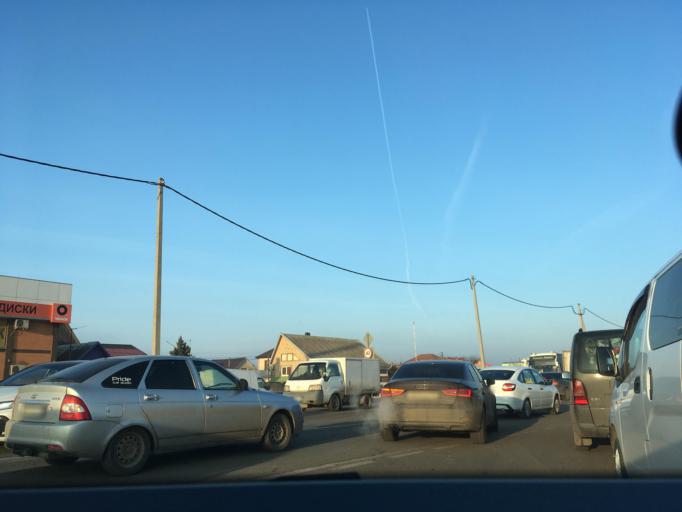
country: RU
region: Krasnodarskiy
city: Krasnodar
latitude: 45.1270
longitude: 39.0117
